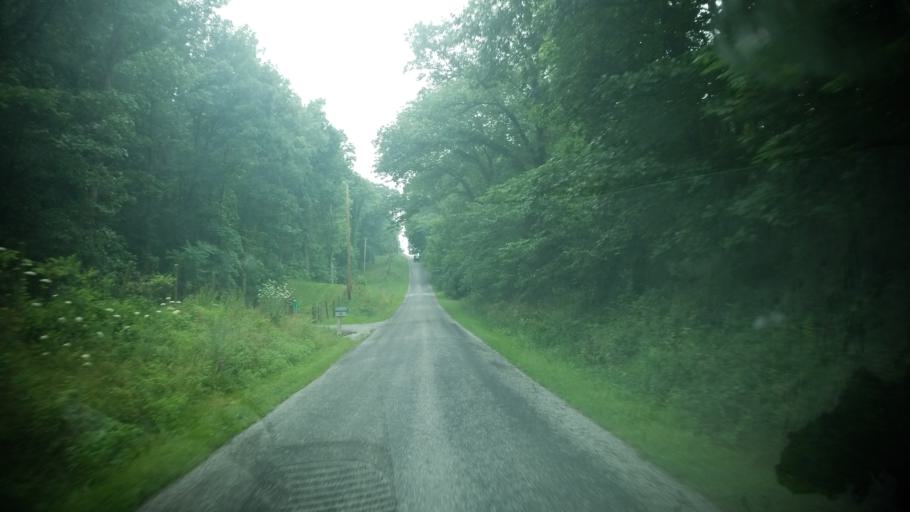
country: US
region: Illinois
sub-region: Clay County
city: Flora
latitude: 38.5735
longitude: -88.3881
